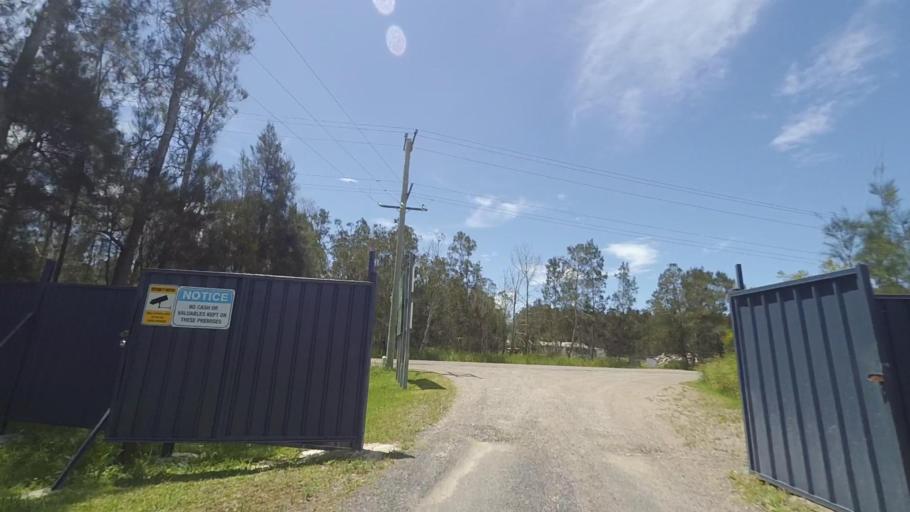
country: AU
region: New South Wales
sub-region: Port Stephens Shire
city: Port Stephens
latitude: -32.7677
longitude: 152.0026
